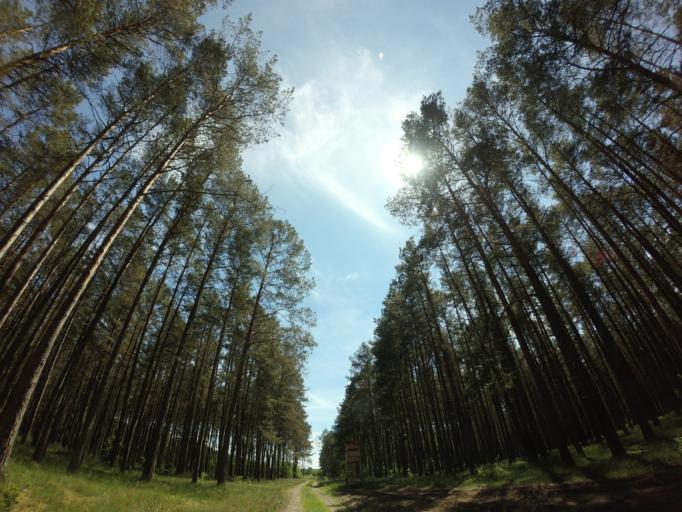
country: PL
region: West Pomeranian Voivodeship
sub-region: Powiat drawski
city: Kalisz Pomorski
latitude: 53.1759
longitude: 15.9018
